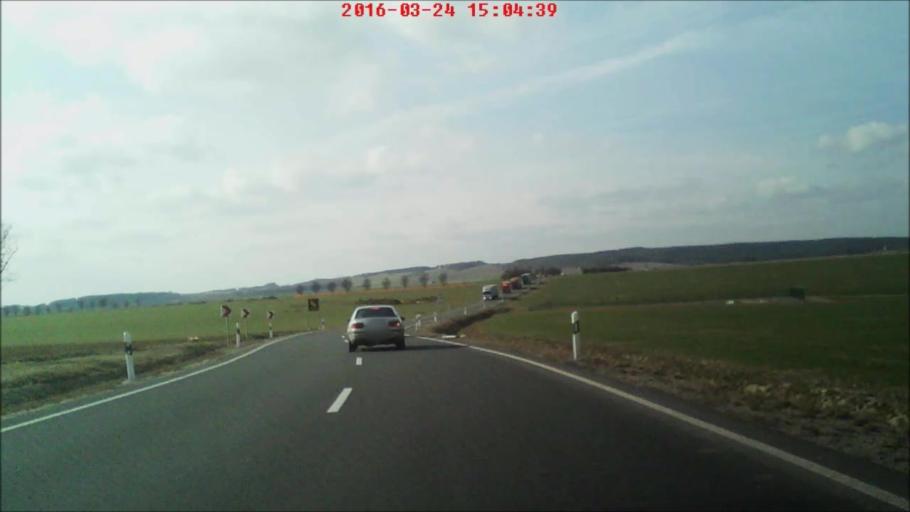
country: DE
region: Thuringia
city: Rottenbach
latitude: 50.7365
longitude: 11.1647
